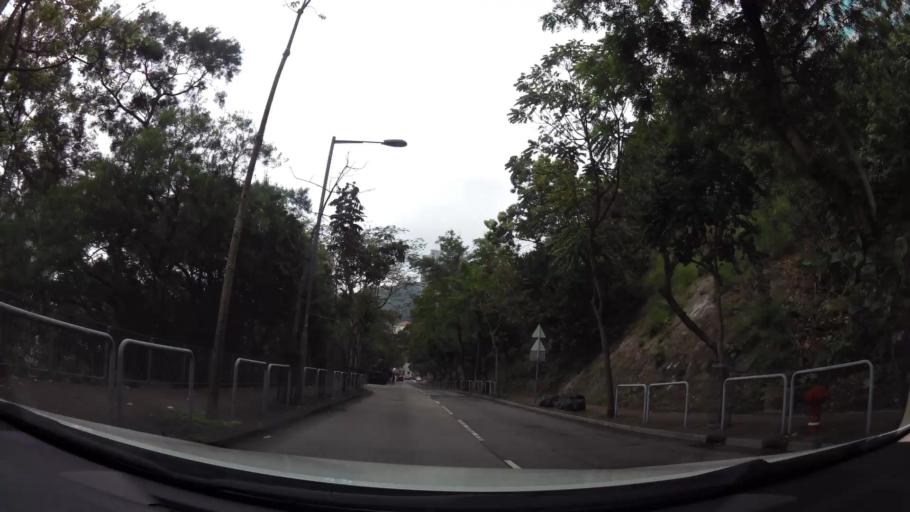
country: HK
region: Central and Western
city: Central
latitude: 22.2669
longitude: 114.1277
